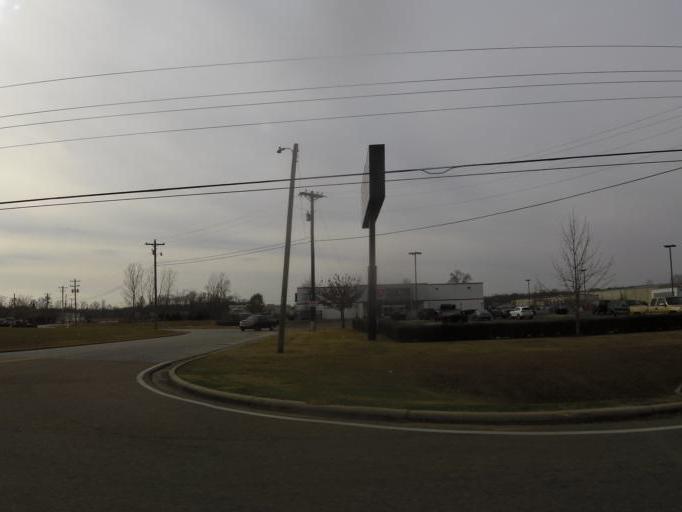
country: US
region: Alabama
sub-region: Montgomery County
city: Pike Road
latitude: 32.3021
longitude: -86.2067
